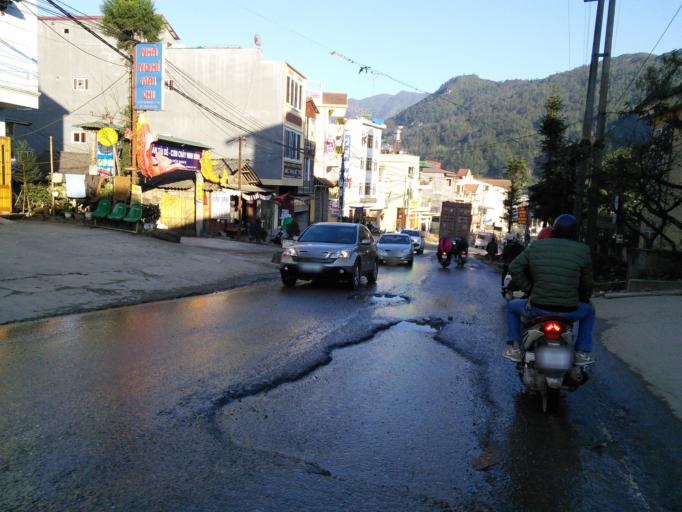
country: VN
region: Lao Cai
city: Sa Pa
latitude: 22.3400
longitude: 103.8468
